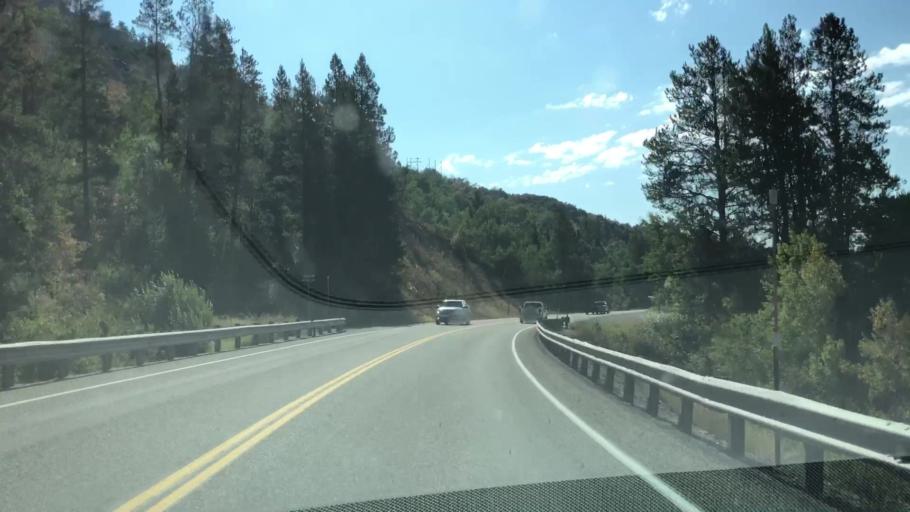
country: US
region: Idaho
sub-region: Teton County
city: Victor
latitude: 43.3252
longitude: -111.1684
